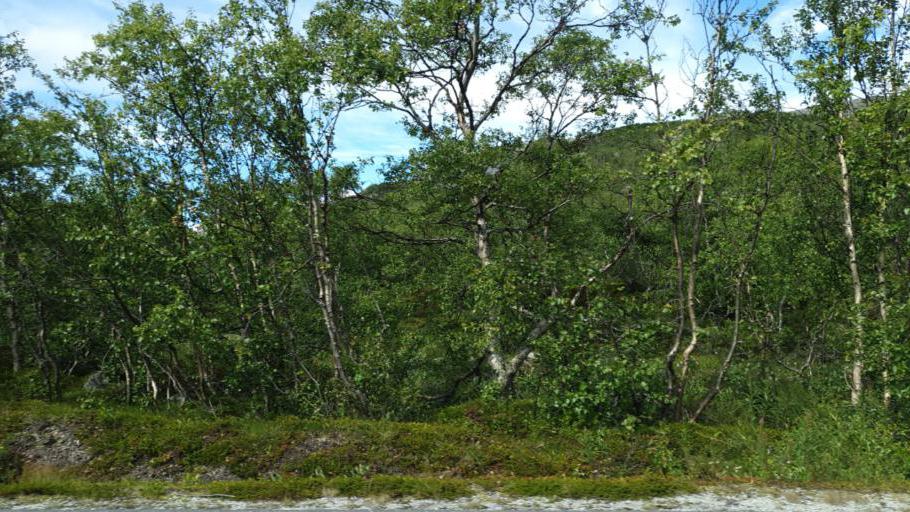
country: NO
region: Oppland
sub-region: Oystre Slidre
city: Heggenes
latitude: 61.4905
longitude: 8.8406
